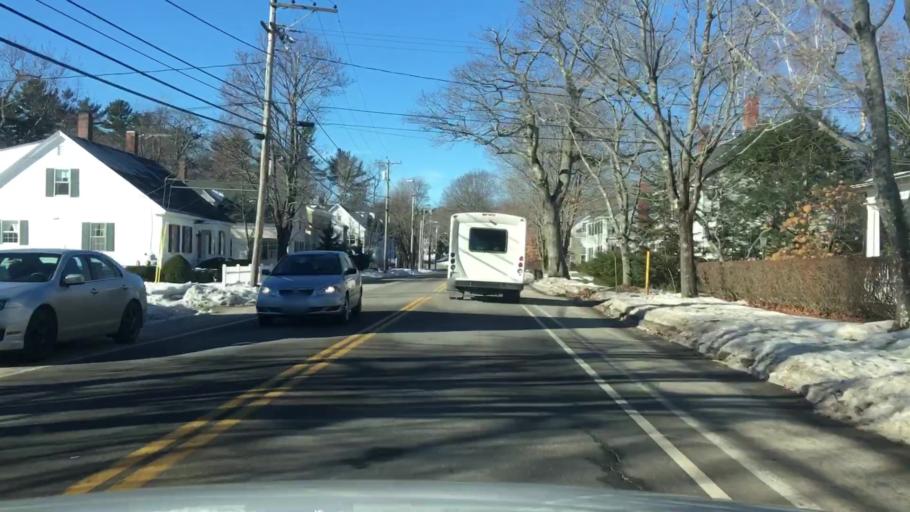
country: US
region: Maine
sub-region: Cumberland County
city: Brunswick
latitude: 43.9263
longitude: -69.9561
